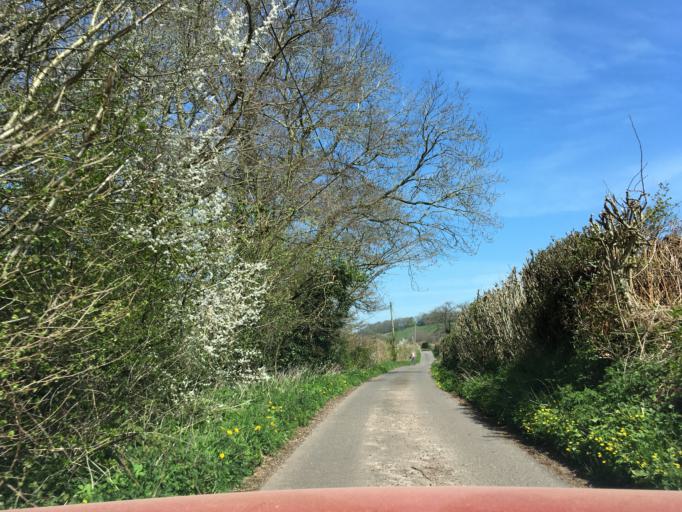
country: GB
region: Wales
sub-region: Monmouthshire
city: Llangwm
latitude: 51.6997
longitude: -2.8300
